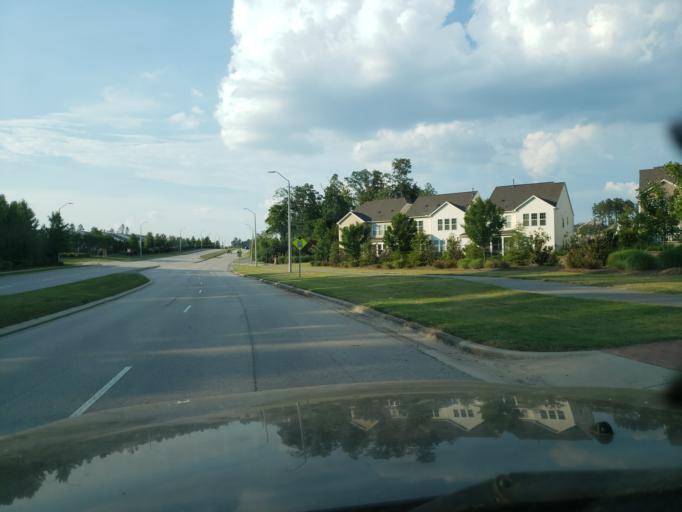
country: US
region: North Carolina
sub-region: Wake County
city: Green Level
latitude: 35.8386
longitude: -78.9106
